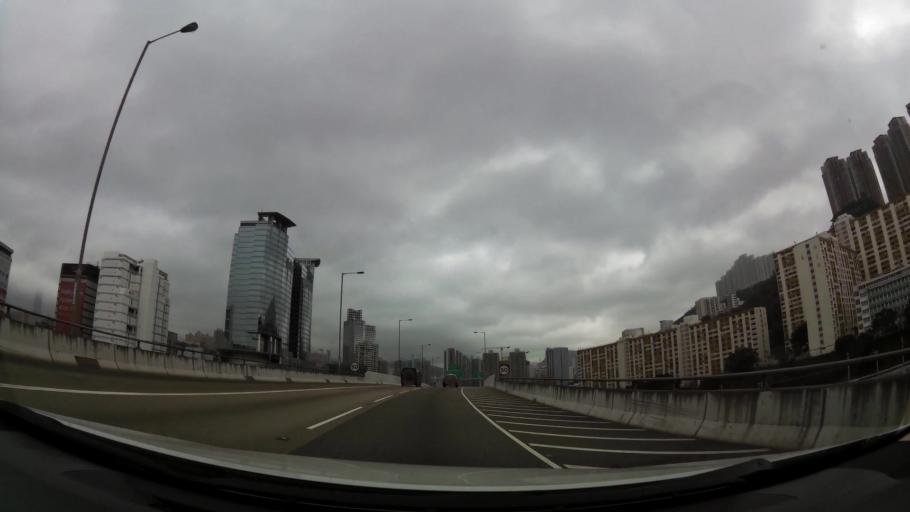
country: HK
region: Tsuen Wan
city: Tsuen Wan
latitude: 22.3498
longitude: 114.1243
